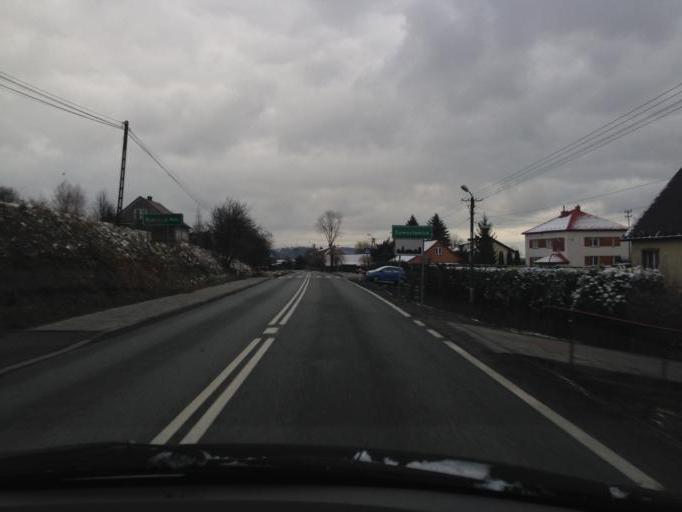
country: PL
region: Lesser Poland Voivodeship
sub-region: Powiat brzeski
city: Zlota
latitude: 49.8614
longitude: 20.7178
